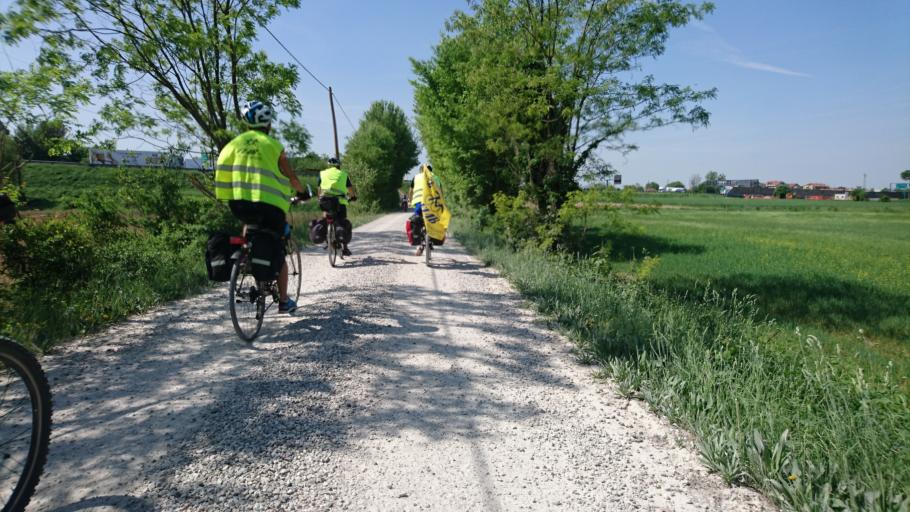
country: IT
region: Veneto
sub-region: Provincia di Padova
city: Vigodarzere
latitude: 45.4431
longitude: 11.8833
